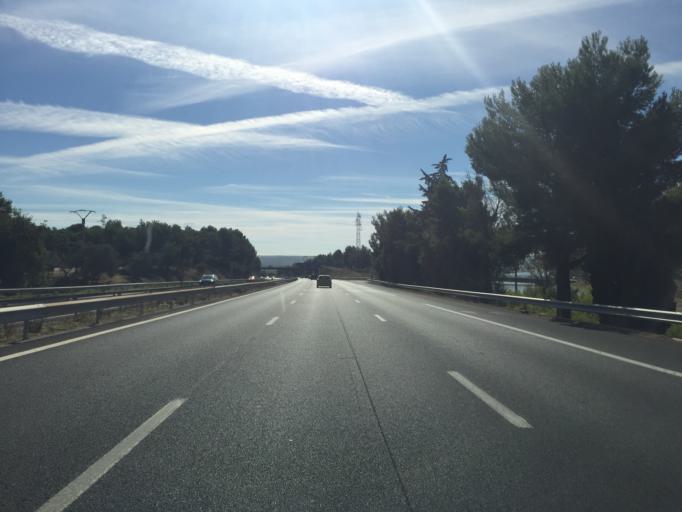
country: FR
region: Provence-Alpes-Cote d'Azur
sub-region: Departement des Bouches-du-Rhone
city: Salon-de-Provence
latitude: 43.6413
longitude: 5.1148
